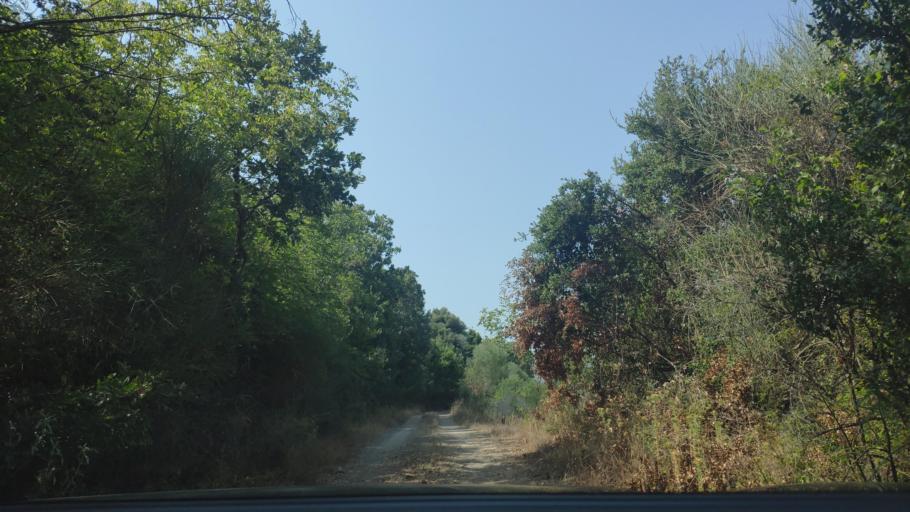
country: GR
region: West Greece
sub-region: Nomos Aitolias kai Akarnanias
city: Fitiai
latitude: 38.7307
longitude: 21.1841
